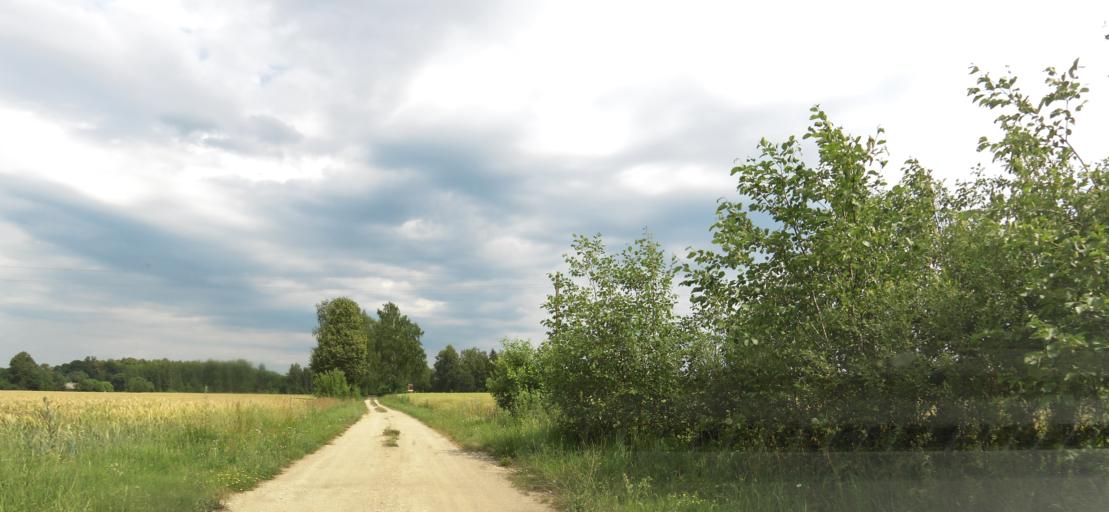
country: LT
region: Panevezys
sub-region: Birzai
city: Birzai
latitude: 56.3286
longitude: 24.9627
